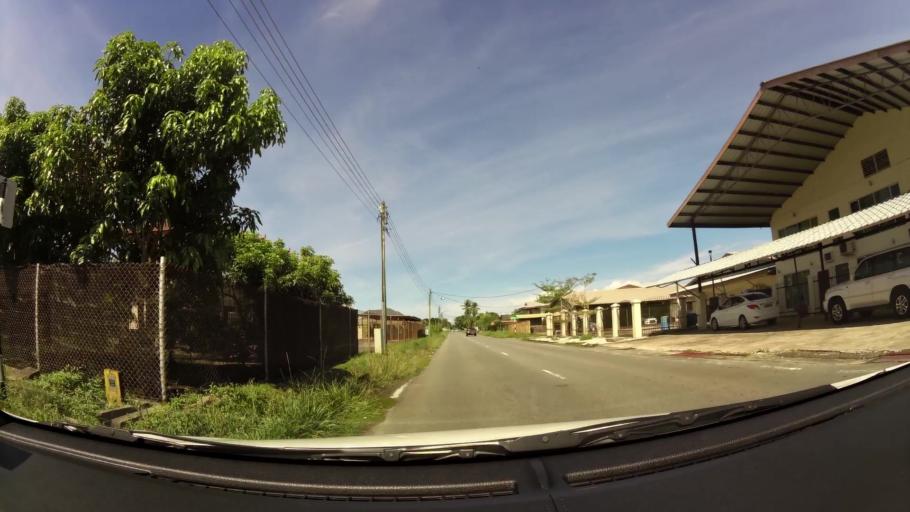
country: BN
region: Belait
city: Kuala Belait
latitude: 4.5867
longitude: 114.2118
